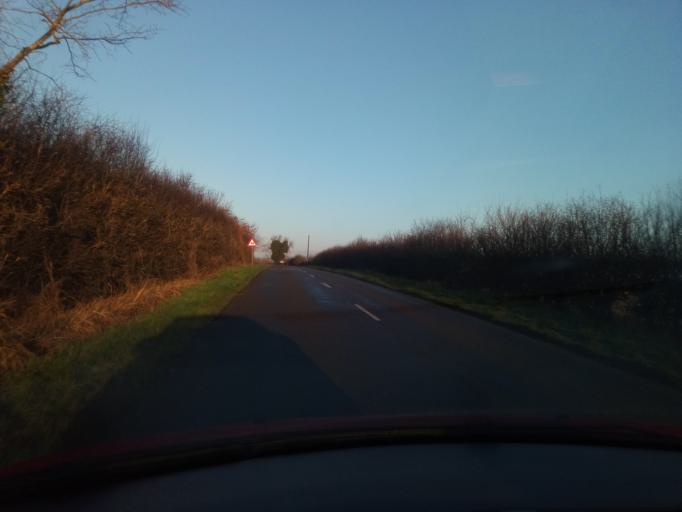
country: GB
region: England
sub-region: Leicestershire
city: Barrow upon Soar
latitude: 52.7696
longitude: -1.1174
